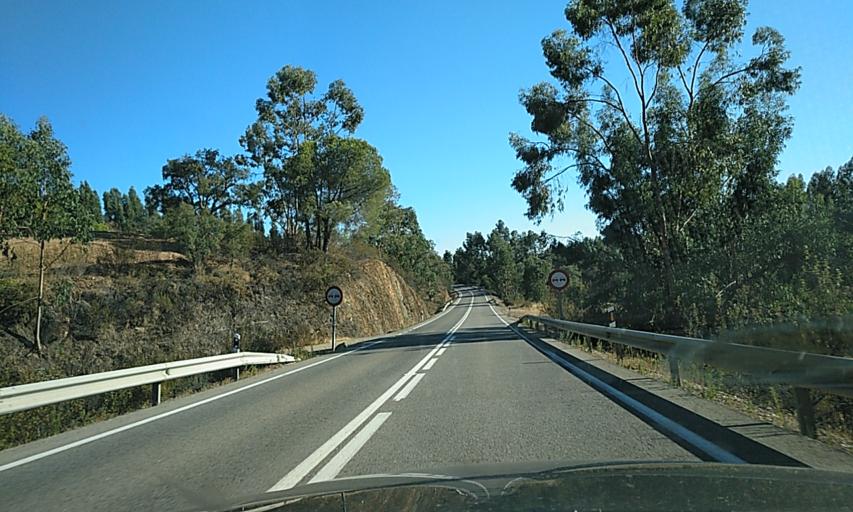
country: ES
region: Andalusia
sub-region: Provincia de Huelva
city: Santa Barbara de Casa
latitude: 37.8312
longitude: -7.2068
